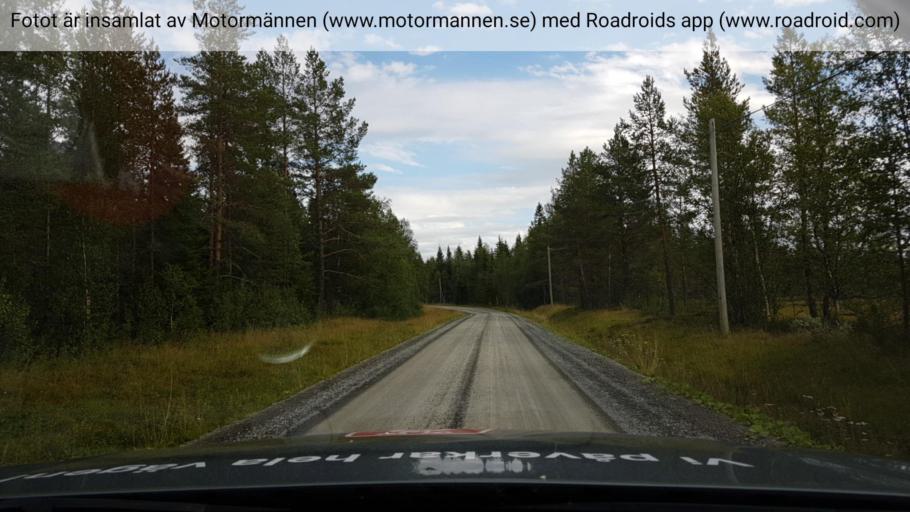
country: SE
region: Jaemtland
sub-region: Krokoms Kommun
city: Valla
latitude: 63.7074
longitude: 13.5608
